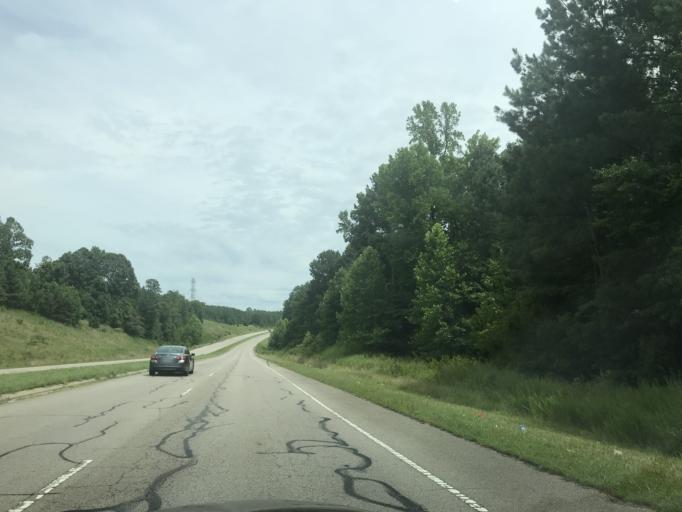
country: US
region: North Carolina
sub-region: Vance County
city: South Henderson
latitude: 36.3037
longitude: -78.4376
